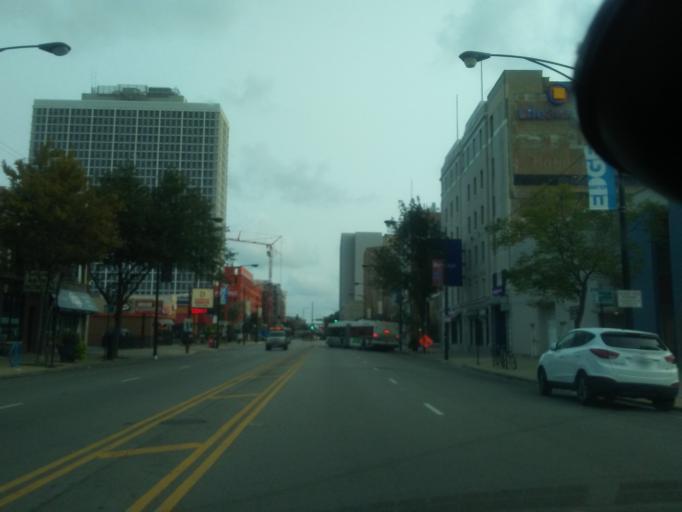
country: US
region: Illinois
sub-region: Cook County
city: Evanston
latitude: 41.9967
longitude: -87.6605
